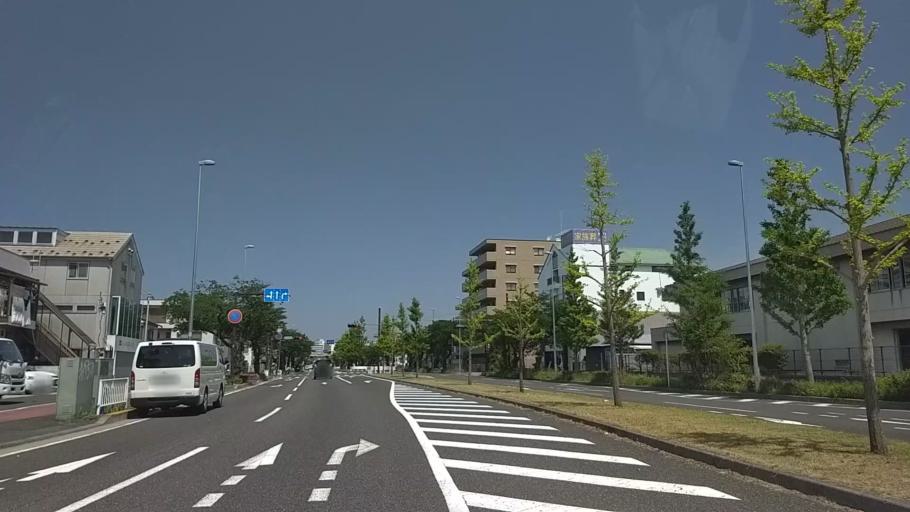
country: JP
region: Kanagawa
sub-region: Kawasaki-shi
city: Kawasaki
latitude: 35.4987
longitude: 139.6874
